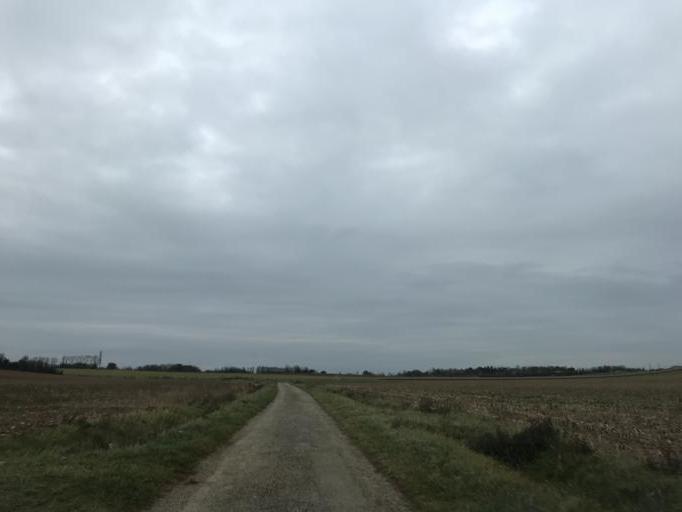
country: FR
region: Rhone-Alpes
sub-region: Departement de l'Ain
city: Miribel
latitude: 45.8421
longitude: 4.9564
